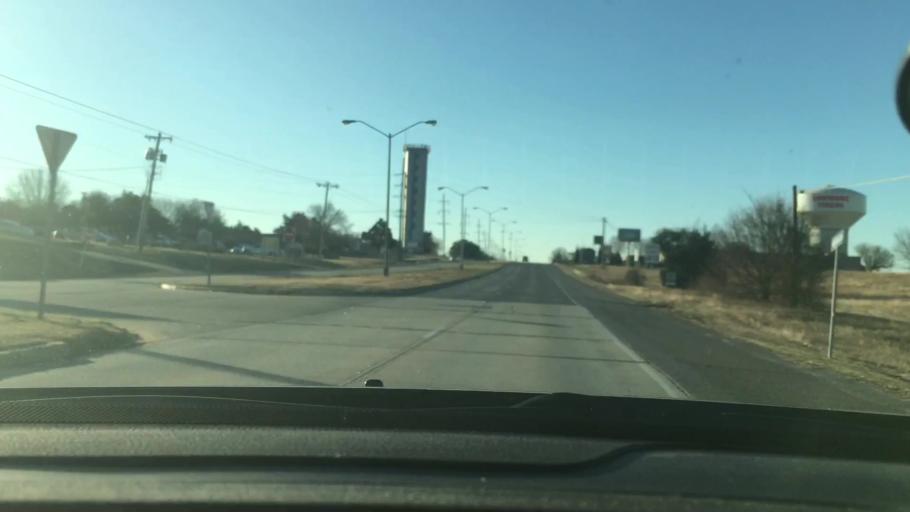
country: US
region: Oklahoma
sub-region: Carter County
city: Ardmore
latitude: 34.2013
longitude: -97.1432
